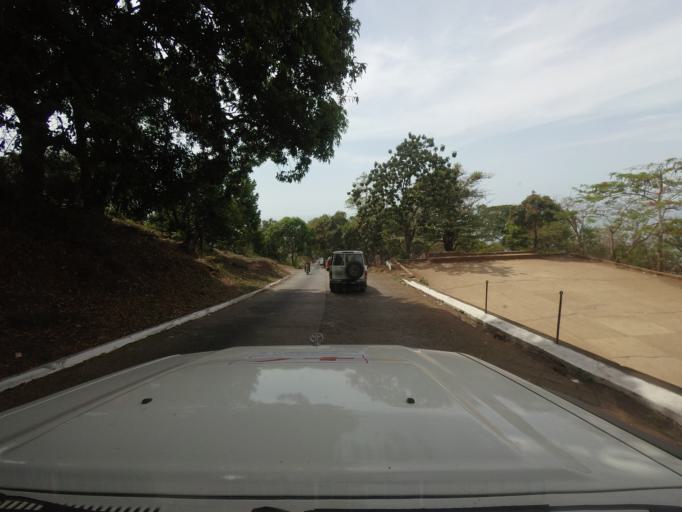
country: SL
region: Western Area
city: Freetown
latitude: 8.4797
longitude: -13.2221
